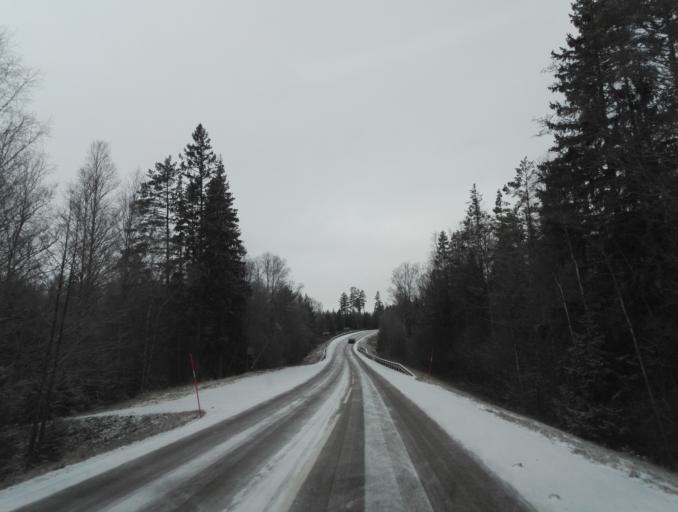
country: SE
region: Kronoberg
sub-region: Lessebo Kommun
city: Lessebo
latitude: 56.8082
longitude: 15.3650
